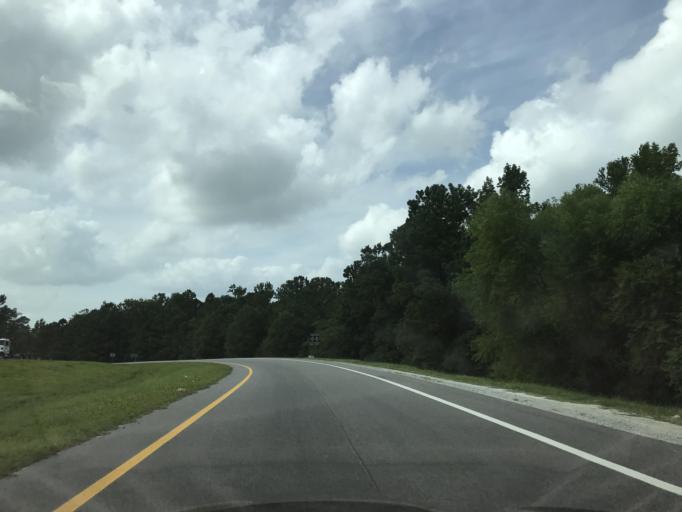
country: US
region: North Carolina
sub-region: New Hanover County
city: Wrightsboro
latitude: 34.3180
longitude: -77.9200
